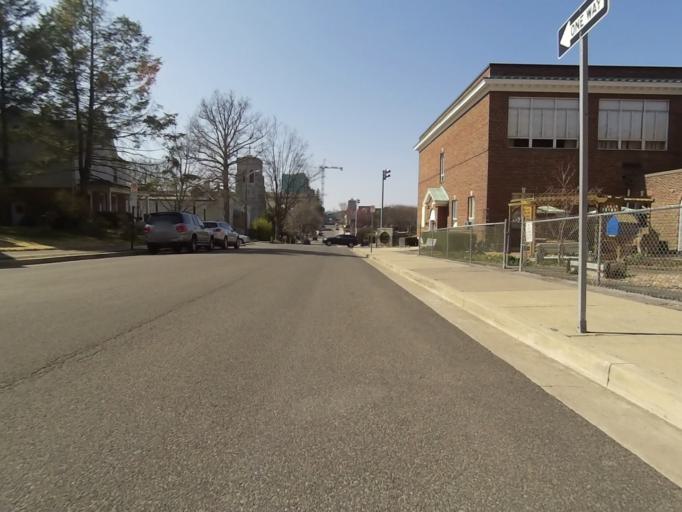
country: US
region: Pennsylvania
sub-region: Centre County
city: State College
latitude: 40.7900
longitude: -77.8584
